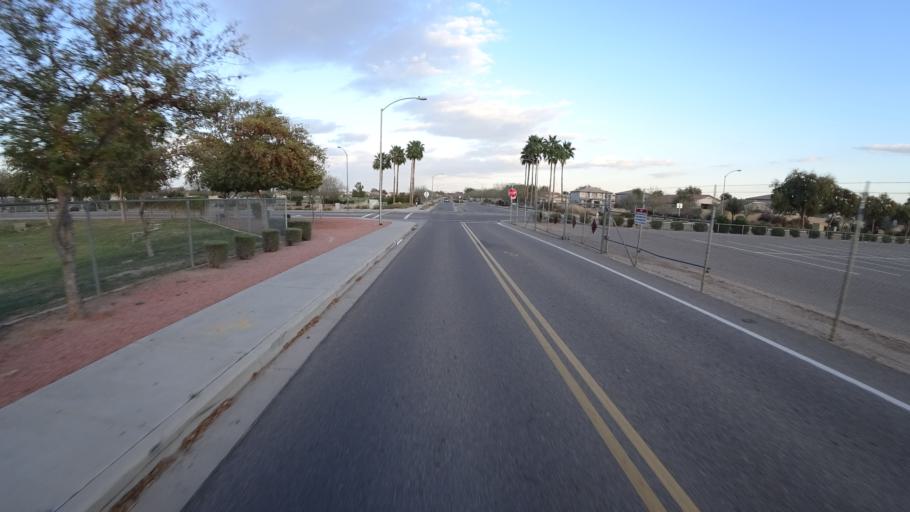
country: US
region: Arizona
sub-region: Maricopa County
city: Peoria
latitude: 33.5448
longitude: -112.2511
